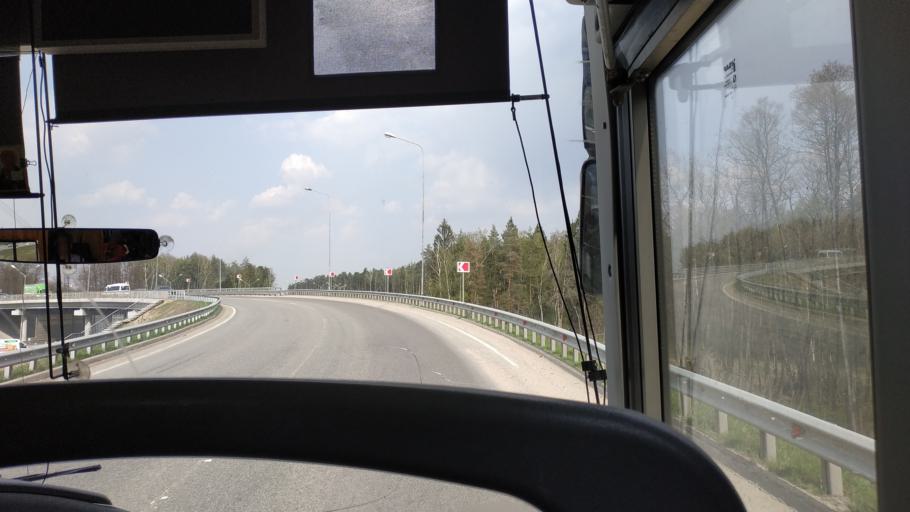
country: RU
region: Moskovskaya
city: Tomilino
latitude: 55.6189
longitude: 37.9287
